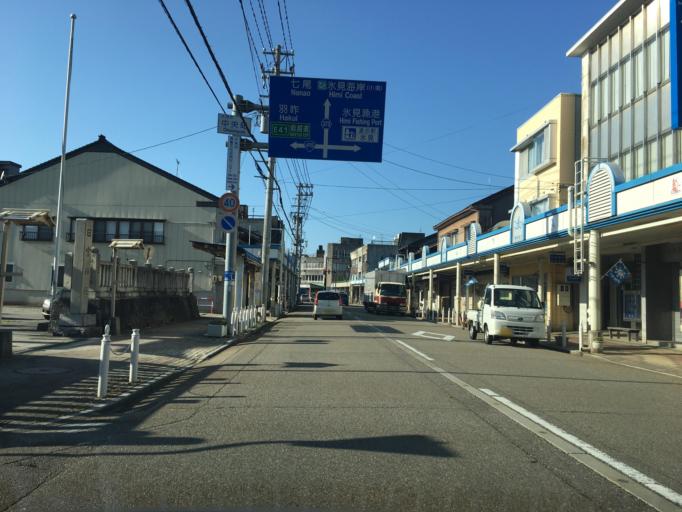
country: JP
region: Toyama
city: Himi
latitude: 36.8582
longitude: 136.9873
